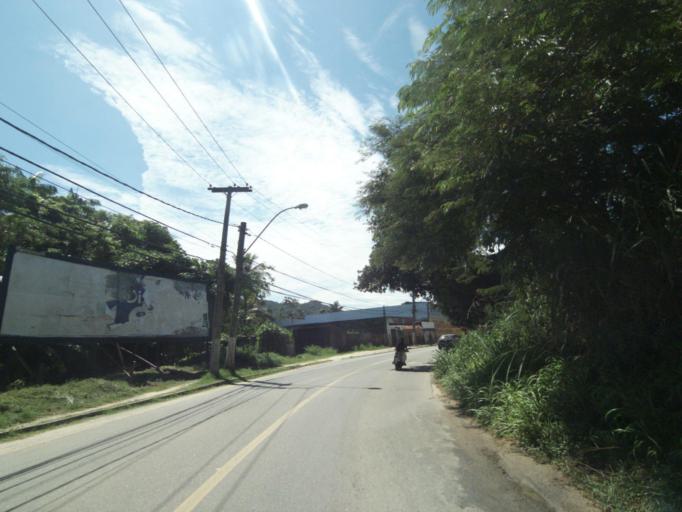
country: BR
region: Rio de Janeiro
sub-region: Niteroi
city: Niteroi
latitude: -22.9312
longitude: -43.0088
